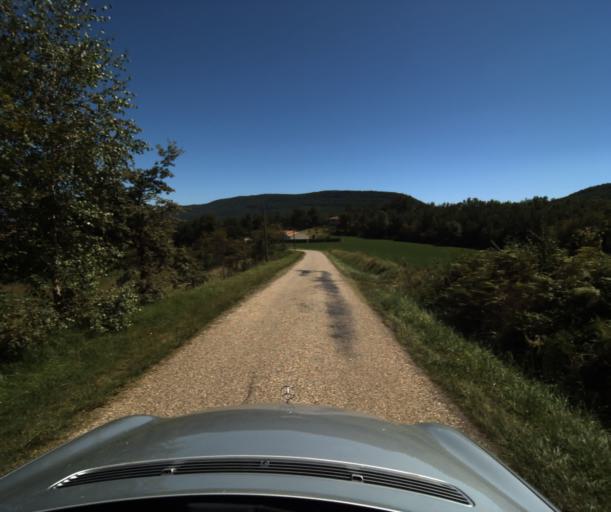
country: FR
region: Midi-Pyrenees
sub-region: Departement de l'Ariege
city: Lavelanet
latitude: 42.9607
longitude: 1.8981
